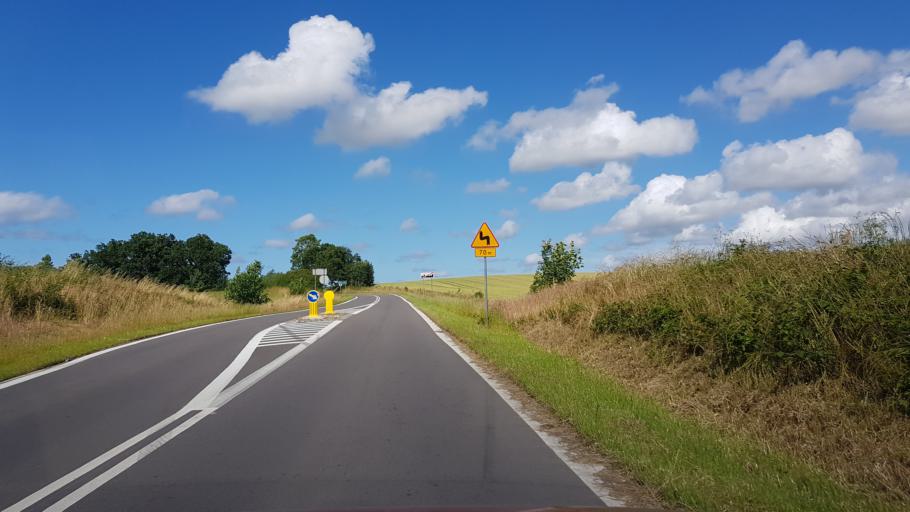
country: PL
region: West Pomeranian Voivodeship
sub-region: Powiat kolobrzeski
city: Ustronie Morskie
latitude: 54.1951
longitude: 15.9058
